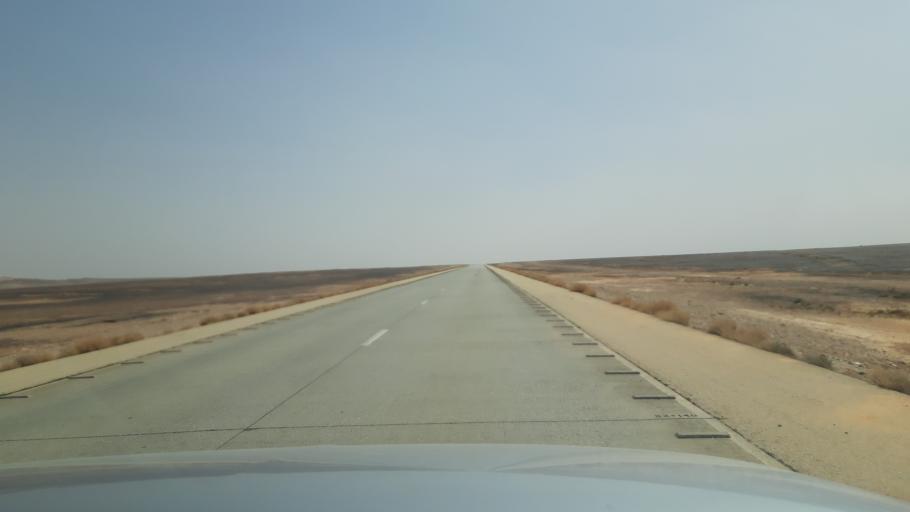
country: SA
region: Al Jawf
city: Al Qurayyat
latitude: 30.9963
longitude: 36.6343
